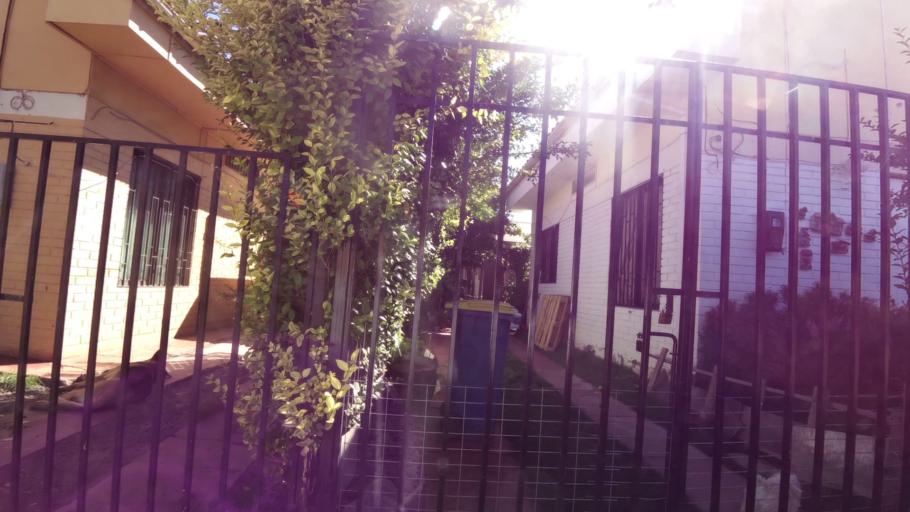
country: CL
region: O'Higgins
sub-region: Provincia de Cachapoal
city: Rancagua
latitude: -34.1780
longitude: -70.7035
